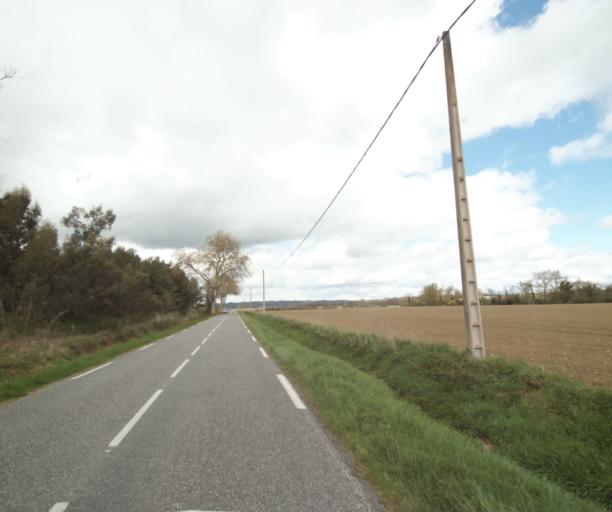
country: FR
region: Midi-Pyrenees
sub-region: Departement de l'Ariege
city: Mazeres
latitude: 43.2421
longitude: 1.6374
